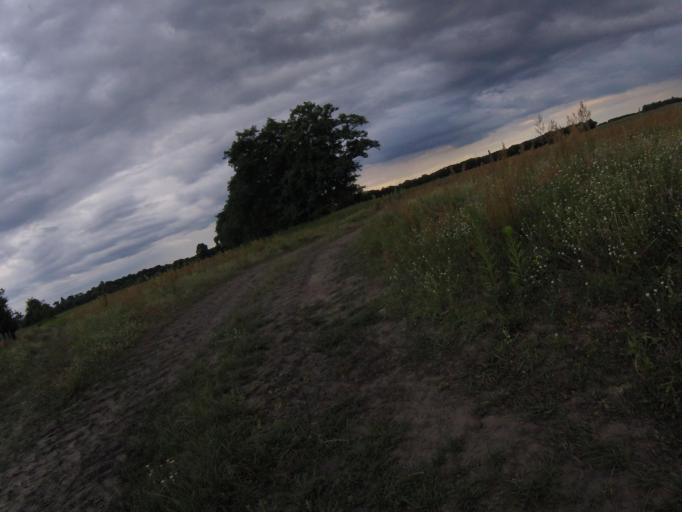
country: DE
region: Brandenburg
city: Mittenwalde
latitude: 52.2777
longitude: 13.5245
